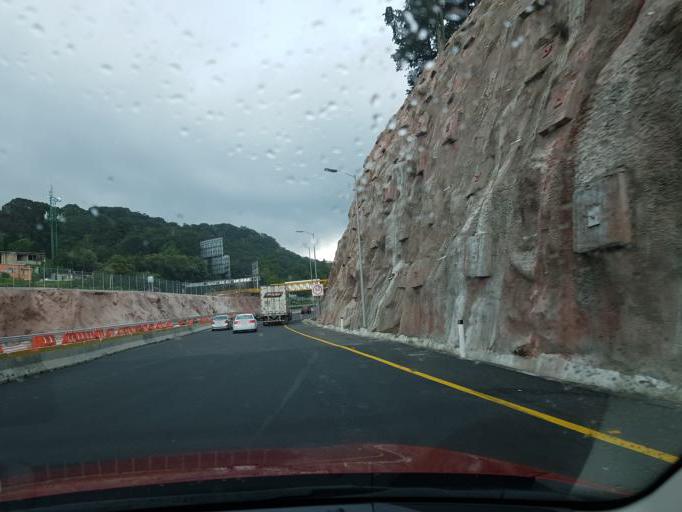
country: MX
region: Mexico
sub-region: Lerma
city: San Miguel Ameyalco
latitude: 19.2911
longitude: -99.4331
